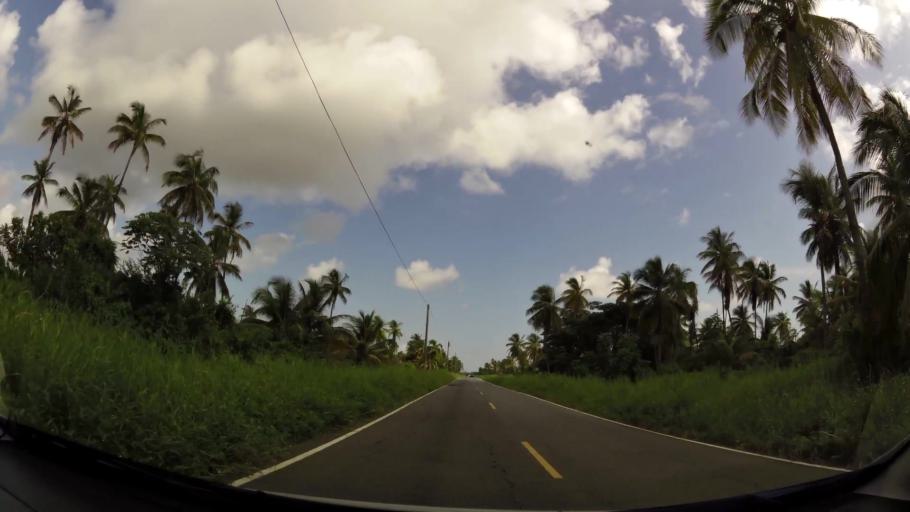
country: GY
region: Demerara-Mahaica
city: Mahaica Village
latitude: 6.7230
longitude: -57.9366
